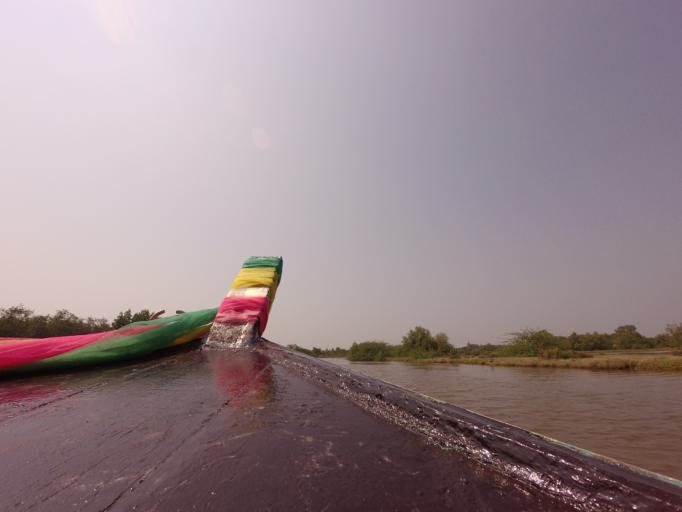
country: TH
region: Prachuap Khiri Khan
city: Kui Buri
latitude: 12.1437
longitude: 99.9496
